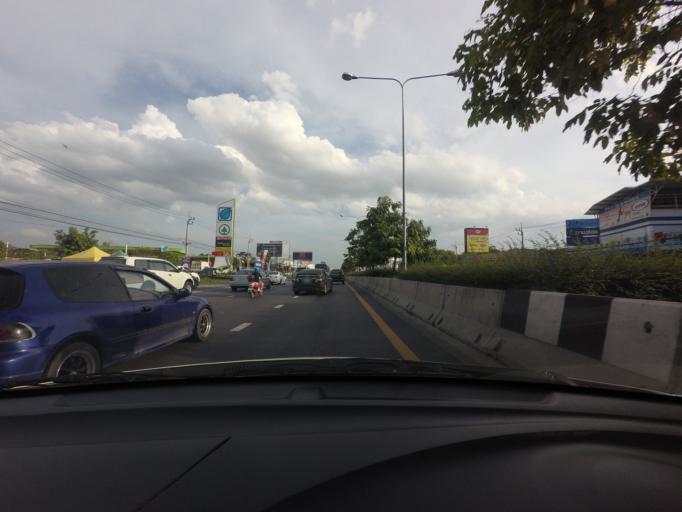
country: TH
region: Nonthaburi
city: Bang Bua Thong
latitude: 13.9157
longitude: 100.4512
